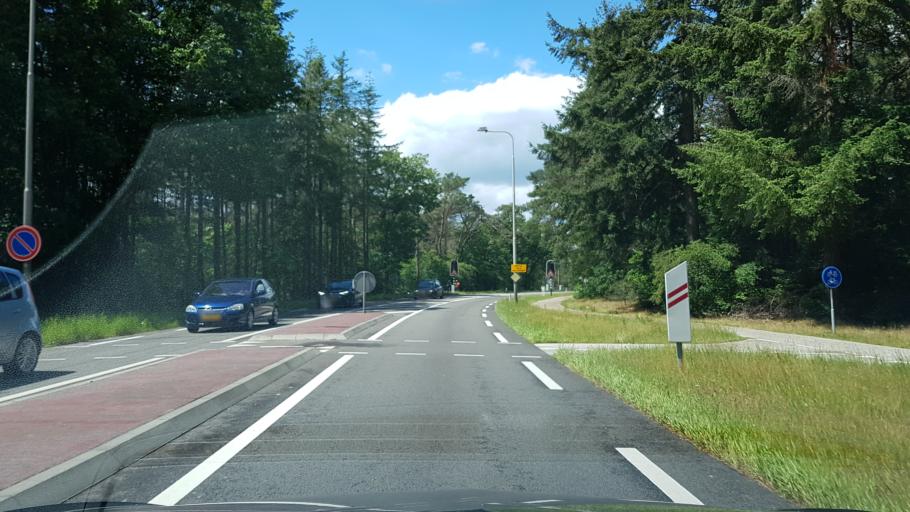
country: NL
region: Gelderland
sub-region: Gemeente Nunspeet
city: Nunspeet
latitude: 52.3763
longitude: 5.8171
